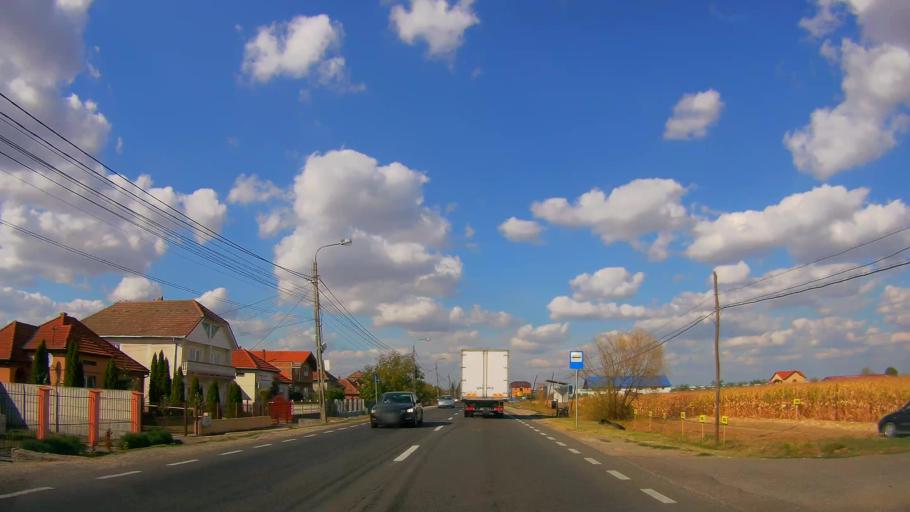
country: RO
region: Satu Mare
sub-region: Comuna Paulesti
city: Paulesti
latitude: 47.7489
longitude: 22.8832
